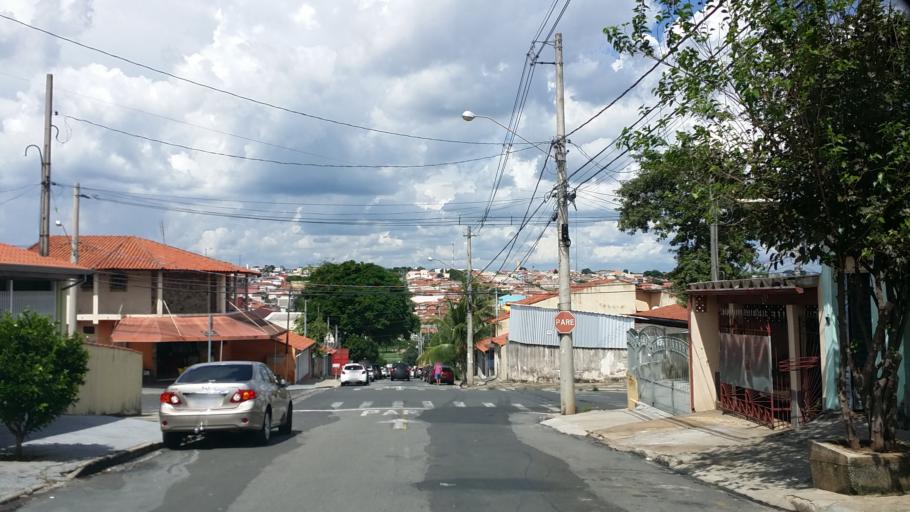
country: BR
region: Sao Paulo
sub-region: Indaiatuba
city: Indaiatuba
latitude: -23.1181
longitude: -47.2364
